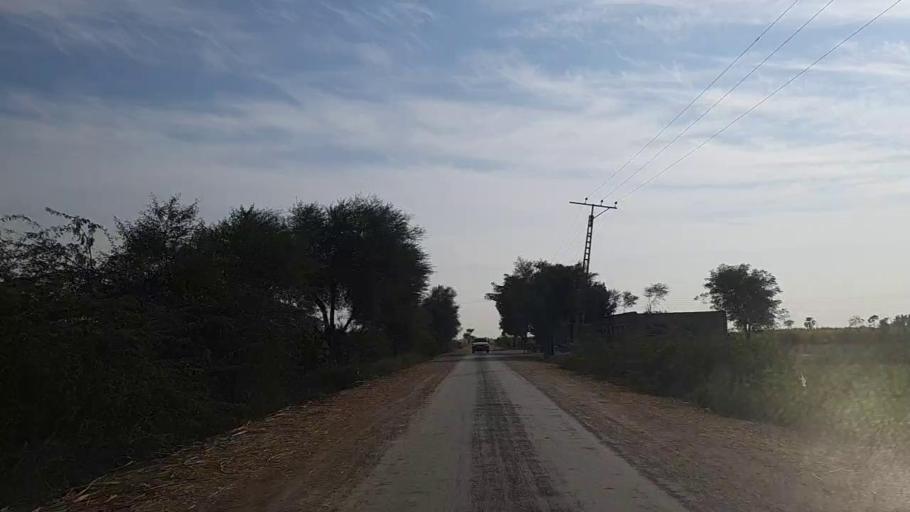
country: PK
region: Sindh
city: Daur
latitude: 26.4860
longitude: 68.4129
